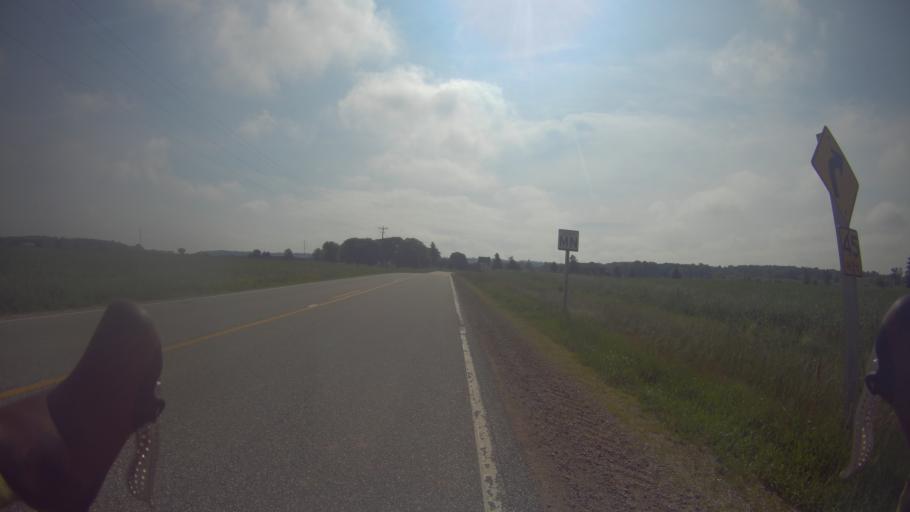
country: US
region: Wisconsin
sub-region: Dane County
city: McFarland
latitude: 43.0150
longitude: -89.2470
